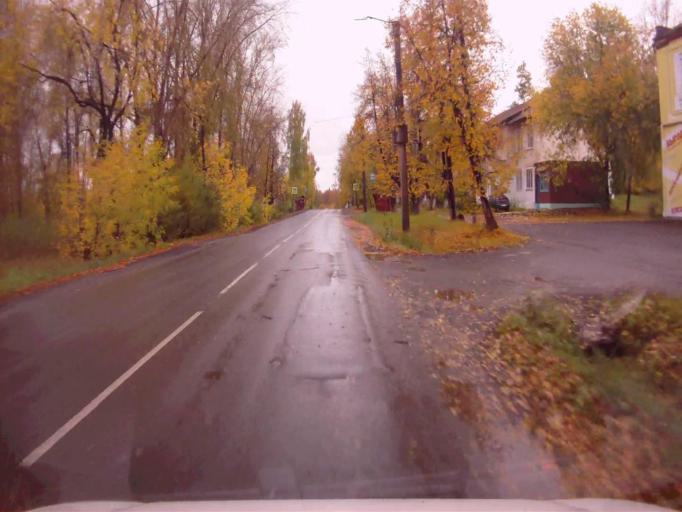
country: RU
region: Chelyabinsk
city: Verkhniy Ufaley
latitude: 56.0399
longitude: 60.2531
